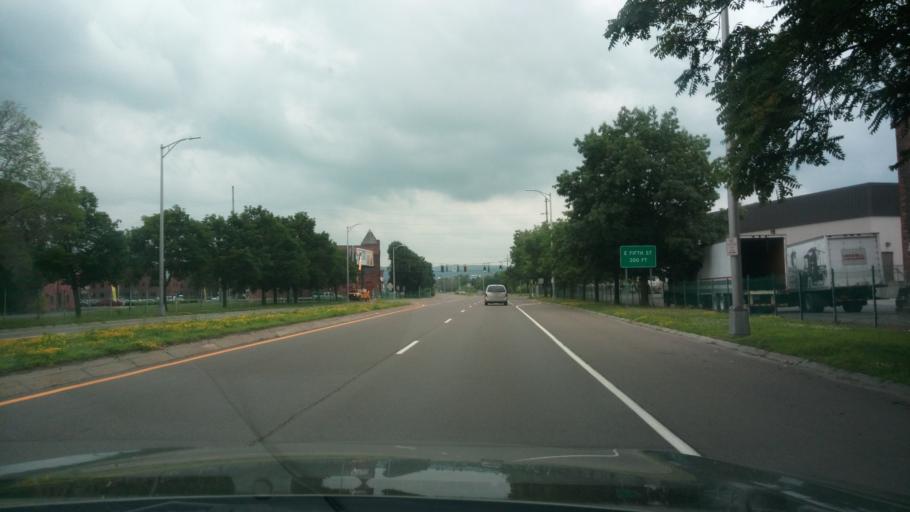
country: US
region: New York
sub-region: Chemung County
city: Elmira
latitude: 42.0982
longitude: -76.8077
